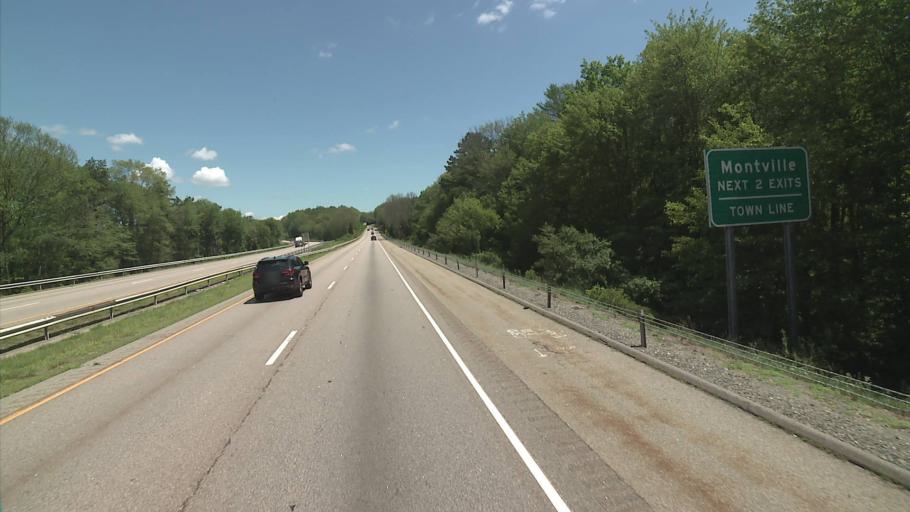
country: US
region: Connecticut
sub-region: New London County
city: Oxoboxo River
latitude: 41.4242
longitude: -72.1279
